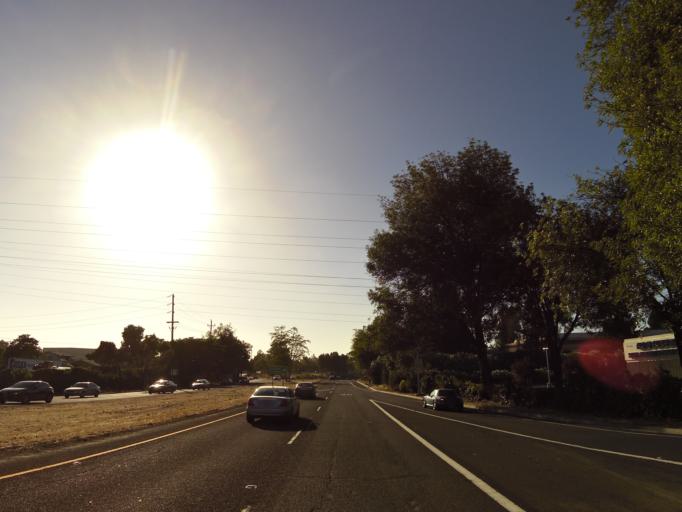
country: US
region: California
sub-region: Santa Clara County
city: Sunnyvale
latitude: 37.3789
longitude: -122.0146
